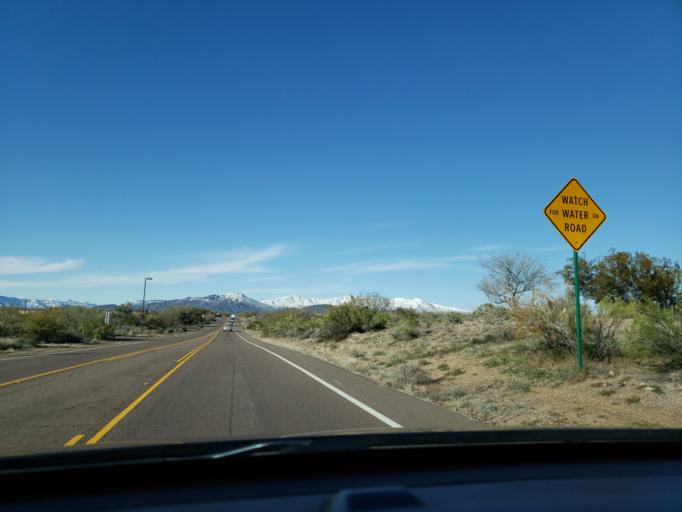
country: US
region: Arizona
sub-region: Maricopa County
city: Carefree
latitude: 33.7740
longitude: -111.8913
